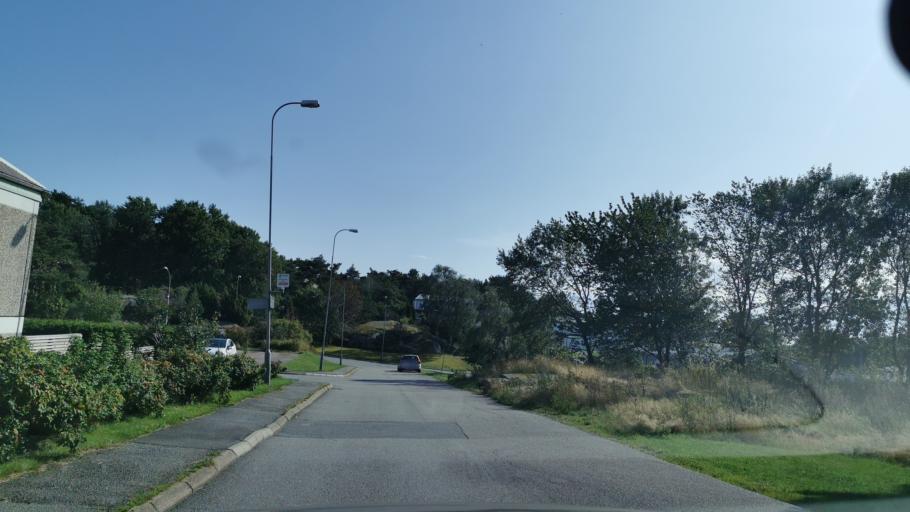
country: SE
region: Vaestra Goetaland
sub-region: Goteborg
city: Majorna
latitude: 57.6422
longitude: 11.9093
